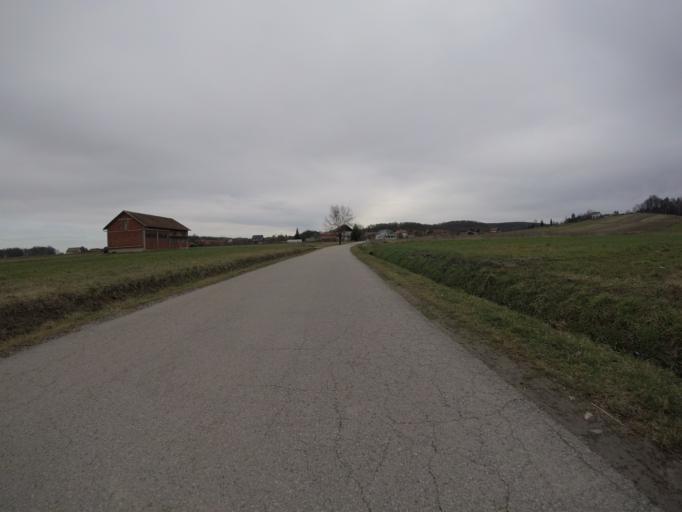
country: HR
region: Grad Zagreb
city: Strmec
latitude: 45.6670
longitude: 15.9195
